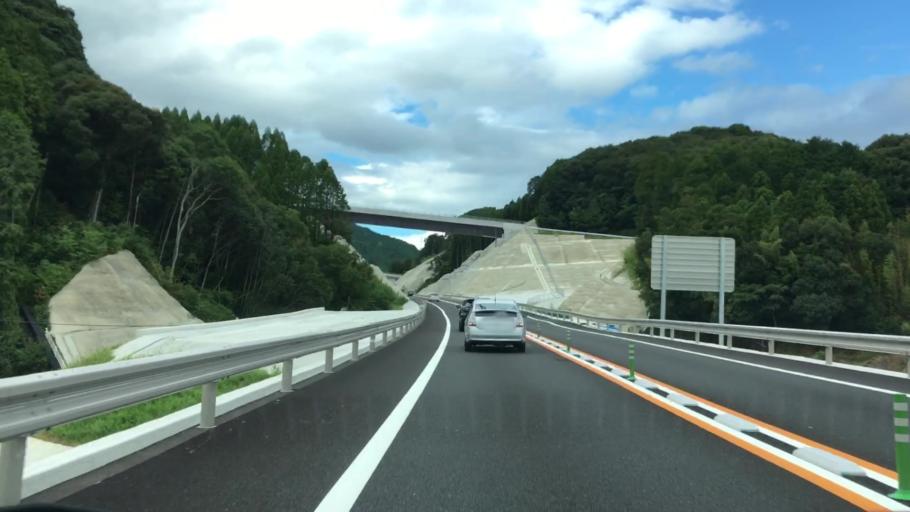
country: JP
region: Saga Prefecture
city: Imaricho-ko
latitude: 33.3020
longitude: 129.9155
